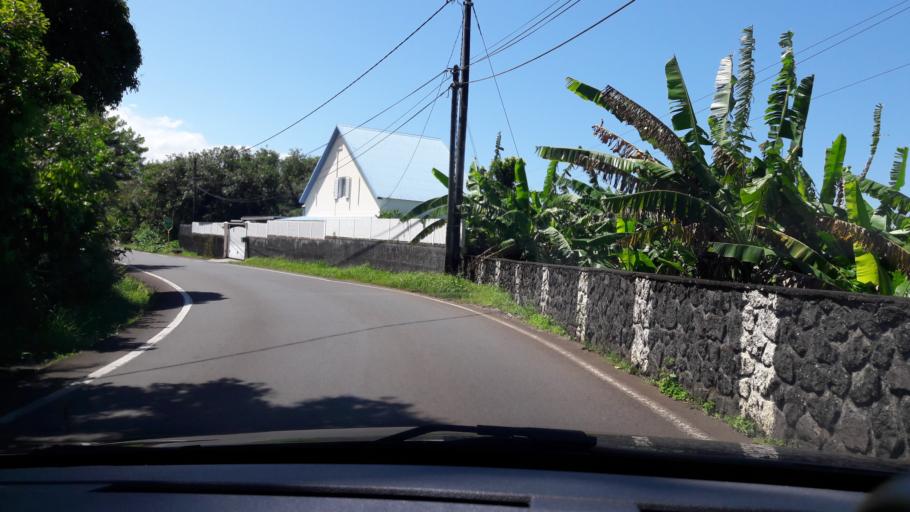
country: RE
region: Reunion
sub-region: Reunion
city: Saint-Benoit
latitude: -21.0952
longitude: 55.7077
